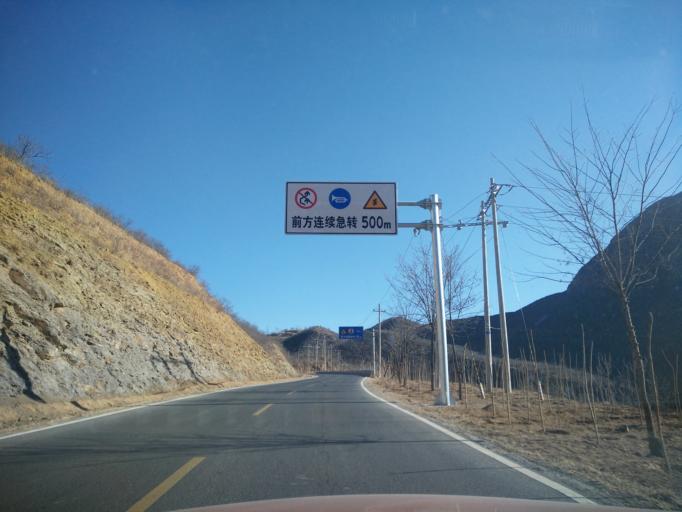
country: CN
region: Beijing
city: Zhaitang
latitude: 40.0072
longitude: 115.6997
